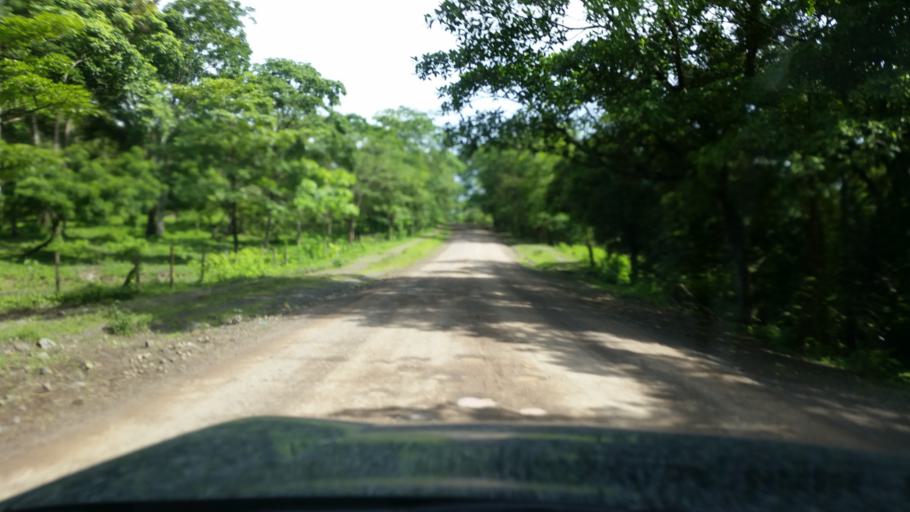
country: NI
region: Atlantico Norte (RAAN)
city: Siuna
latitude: 13.6589
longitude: -84.7933
